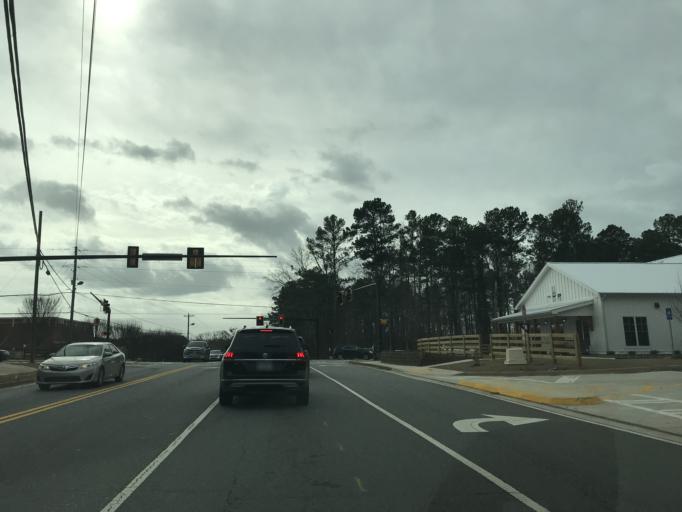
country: US
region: Georgia
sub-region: Fulton County
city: Milton
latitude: 34.1201
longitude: -84.2766
